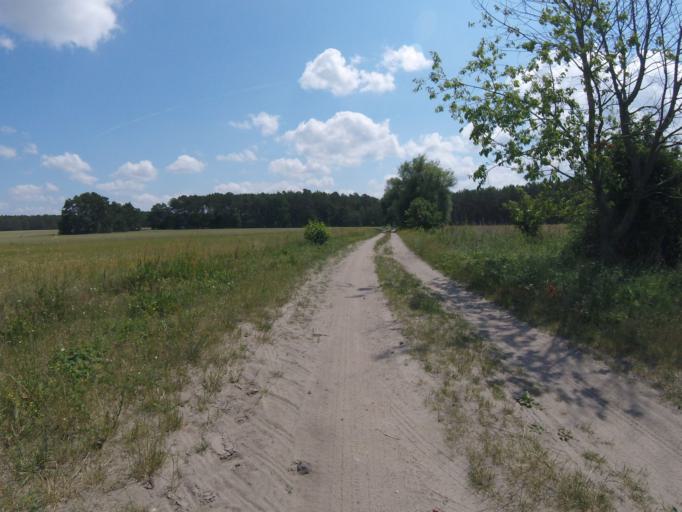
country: DE
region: Brandenburg
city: Bestensee
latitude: 52.2757
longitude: 13.6851
